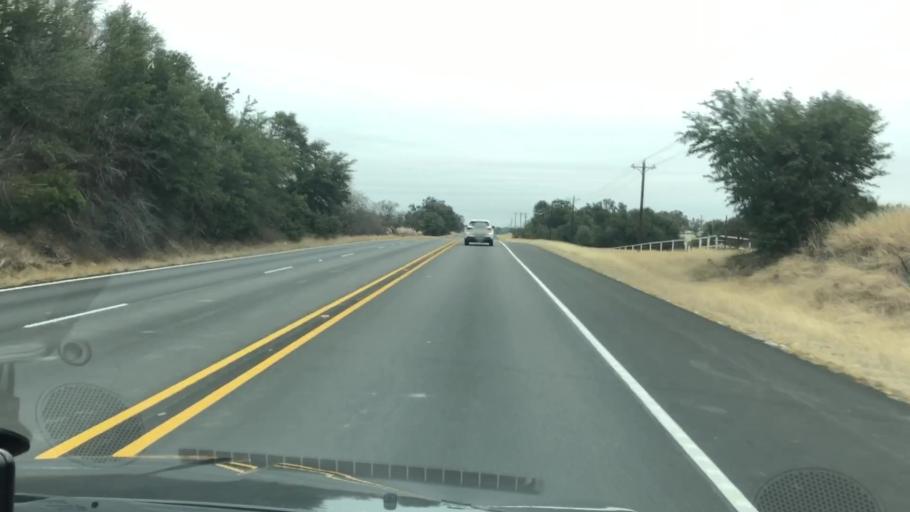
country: US
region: Texas
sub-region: Erath County
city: Stephenville
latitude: 32.3059
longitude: -98.1861
